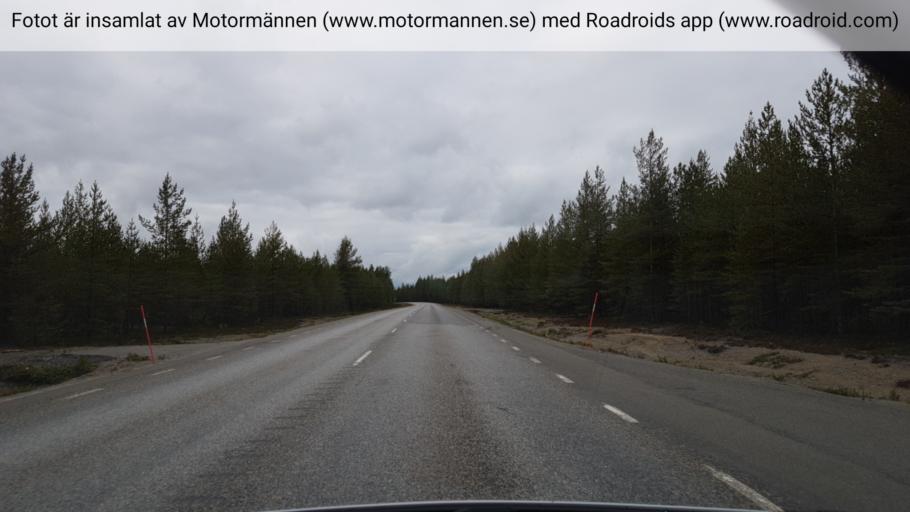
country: SE
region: Vaesterbotten
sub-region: Norsjo Kommun
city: Norsjoe
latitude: 64.9823
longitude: 19.5529
